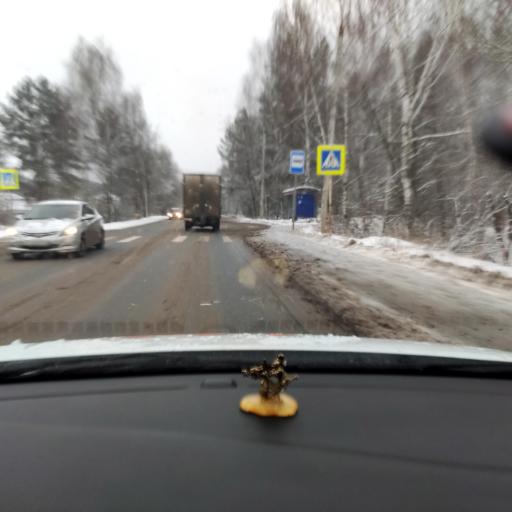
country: RU
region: Tatarstan
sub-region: Zelenodol'skiy Rayon
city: Zelenodolsk
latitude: 55.8668
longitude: 48.5392
